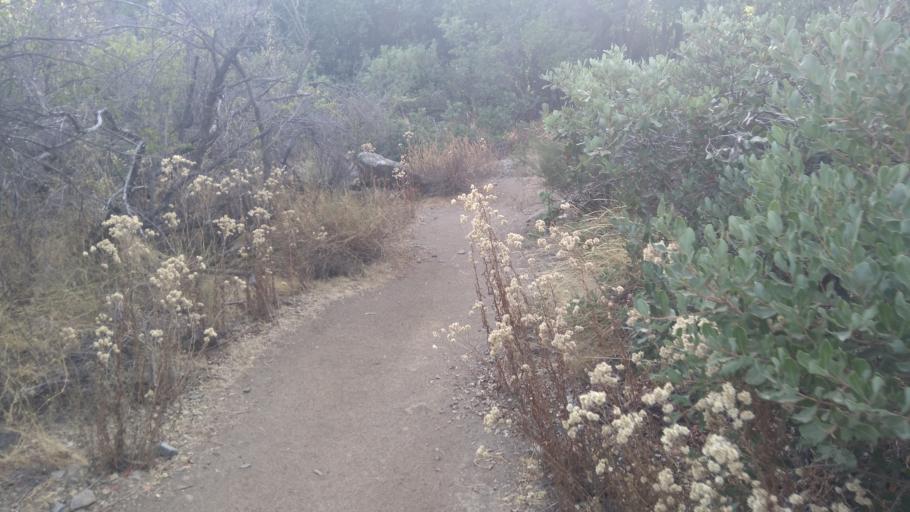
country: CL
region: Santiago Metropolitan
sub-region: Provincia de Cordillera
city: Puente Alto
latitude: -33.7248
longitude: -70.4813
